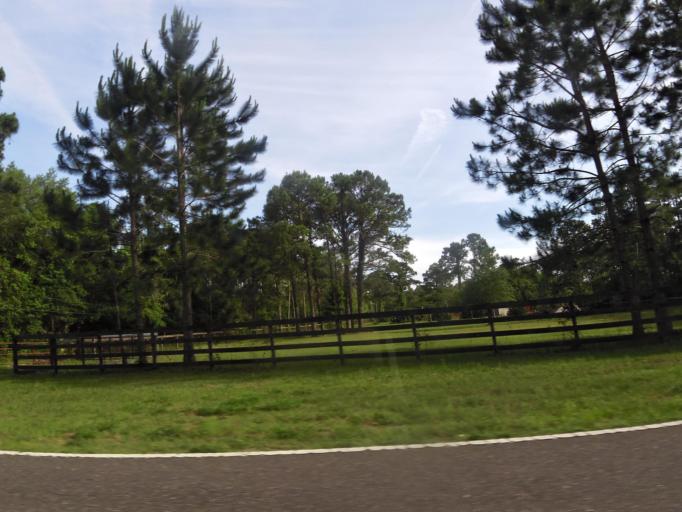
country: US
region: Florida
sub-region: Duval County
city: Atlantic Beach
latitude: 30.4601
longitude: -81.4746
